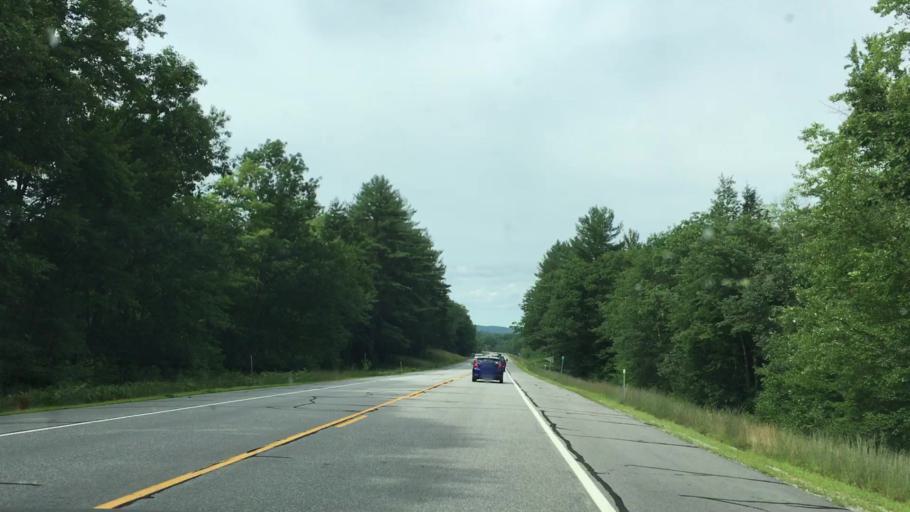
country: US
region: New Hampshire
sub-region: Hillsborough County
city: Hillsborough
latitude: 43.0749
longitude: -71.9171
